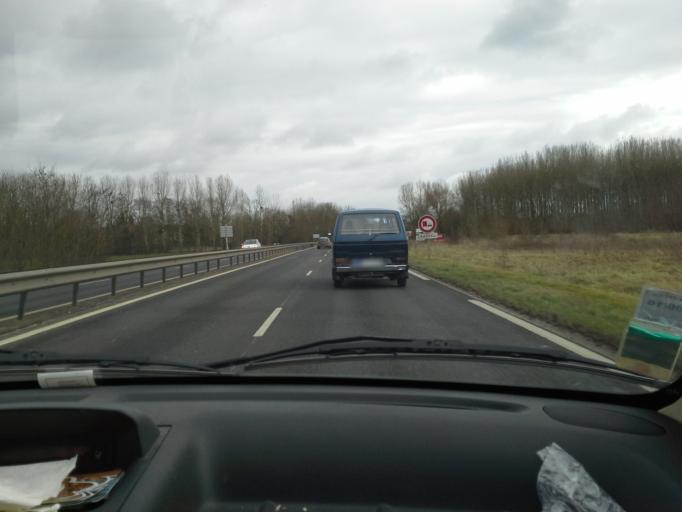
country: FR
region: Centre
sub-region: Departement du Loir-et-Cher
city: Vineuil
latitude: 47.5880
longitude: 1.3615
